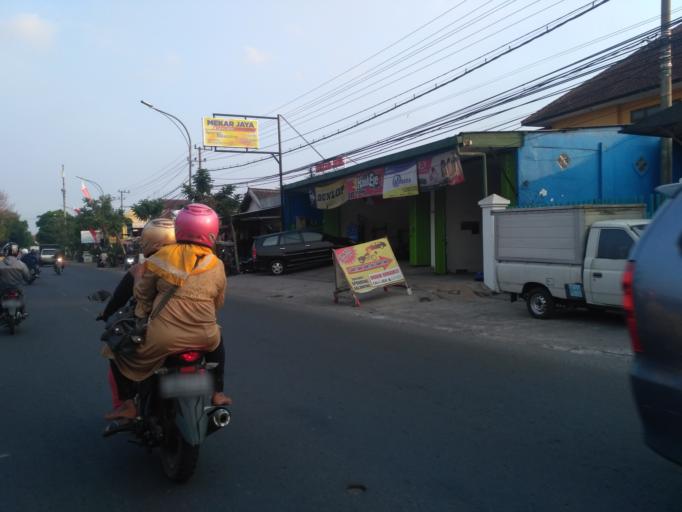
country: ID
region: East Java
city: Kepuh
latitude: -8.0102
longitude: 112.6200
